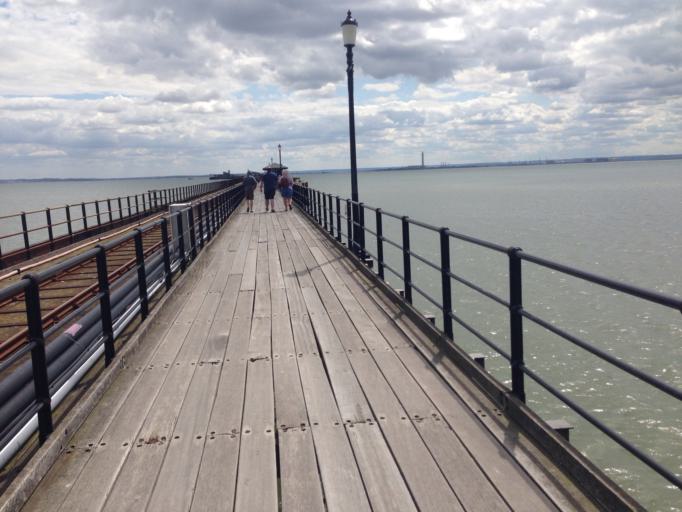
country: GB
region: England
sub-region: Southend-on-Sea
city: Southend-on-Sea
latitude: 51.5265
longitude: 0.7179
